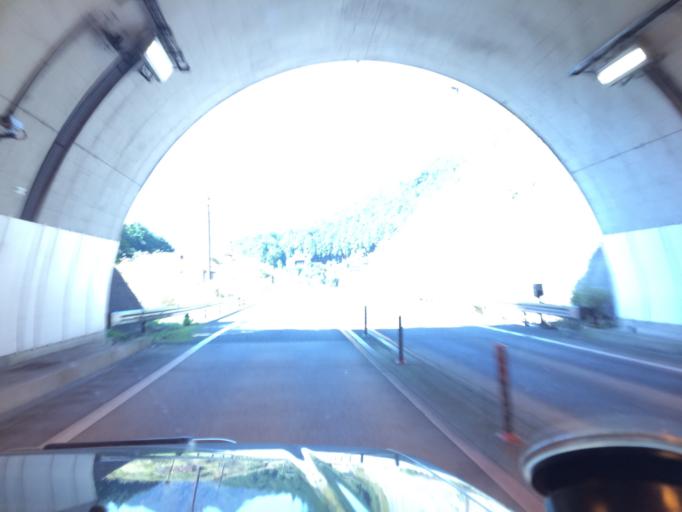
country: JP
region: Kyoto
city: Fukuchiyama
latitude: 35.2649
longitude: 135.0051
